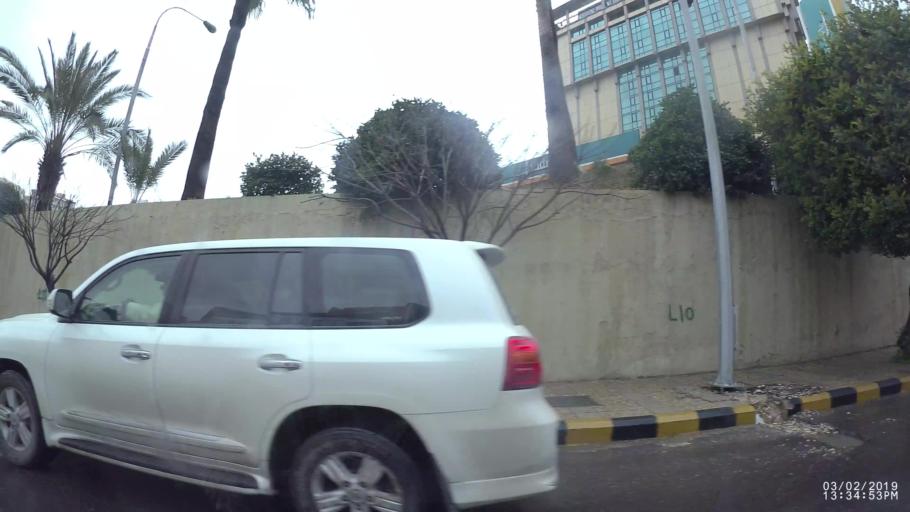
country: JO
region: Amman
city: Amman
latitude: 31.9604
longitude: 35.9048
